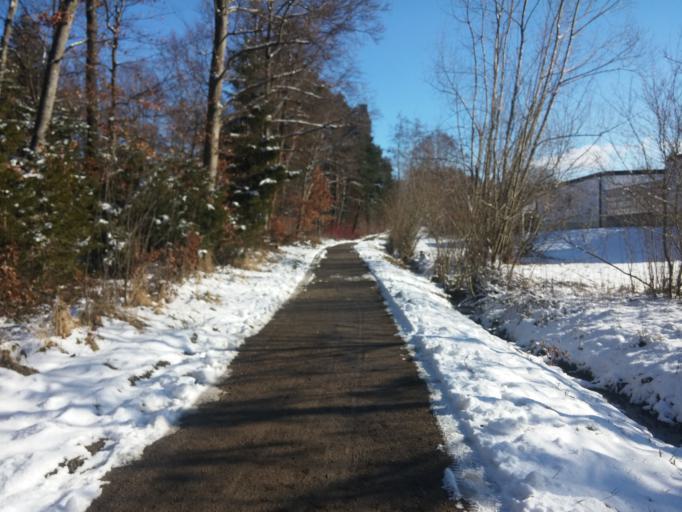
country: DE
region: Baden-Wuerttemberg
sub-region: Tuebingen Region
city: Leutkirch im Allgau
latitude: 47.8313
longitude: 10.0371
